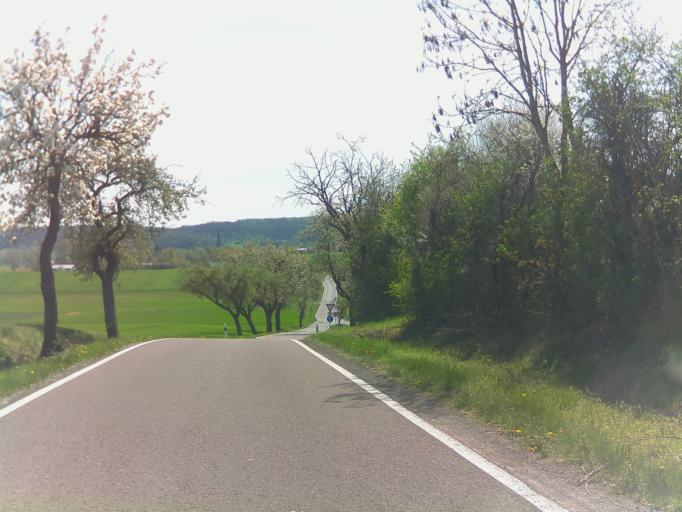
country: DE
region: Thuringia
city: Veilsdorf
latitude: 50.3213
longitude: 10.7997
